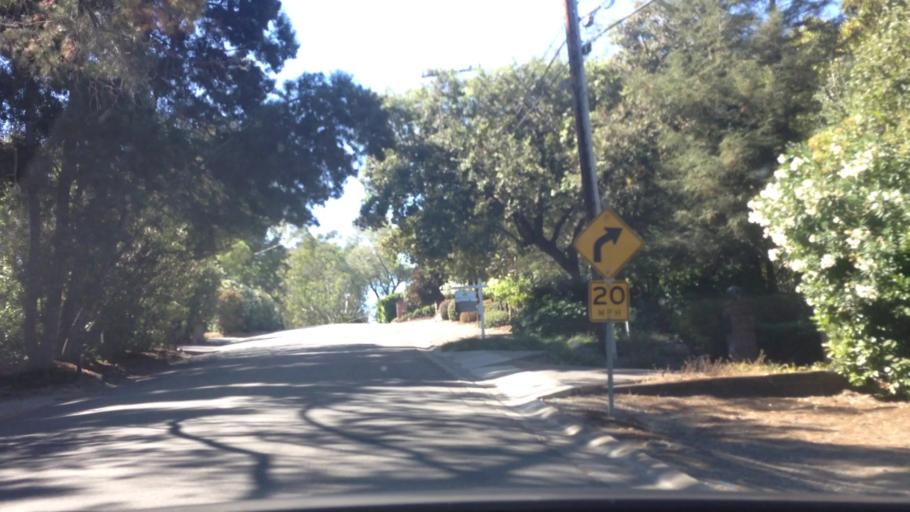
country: US
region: California
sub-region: San Mateo County
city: West Menlo Park
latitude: 37.4378
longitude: -122.2188
